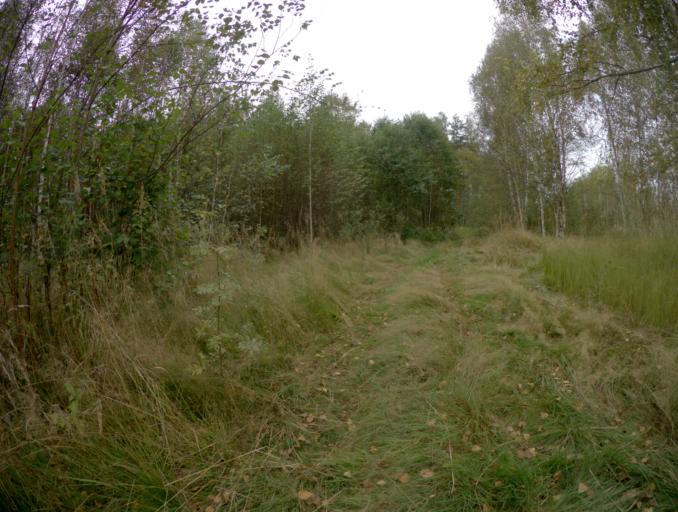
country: RU
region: Vladimir
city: Urshel'skiy
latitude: 55.8207
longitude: 40.2747
